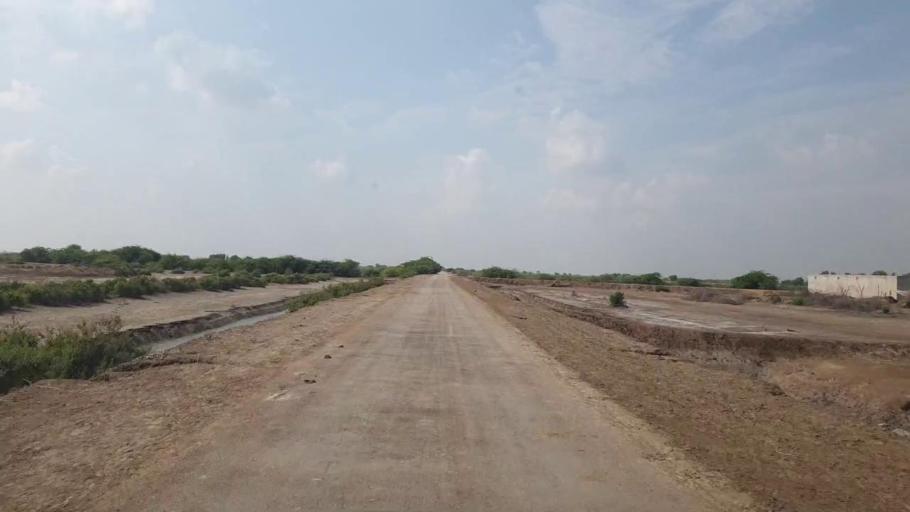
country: PK
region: Sindh
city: Badin
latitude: 24.5066
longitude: 68.6297
